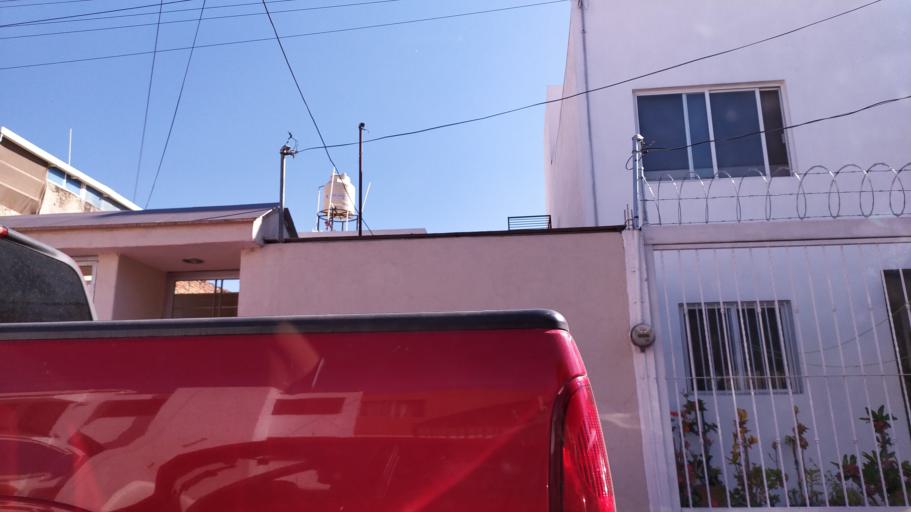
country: MX
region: Jalisco
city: Guadalajara
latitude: 20.6507
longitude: -103.4430
